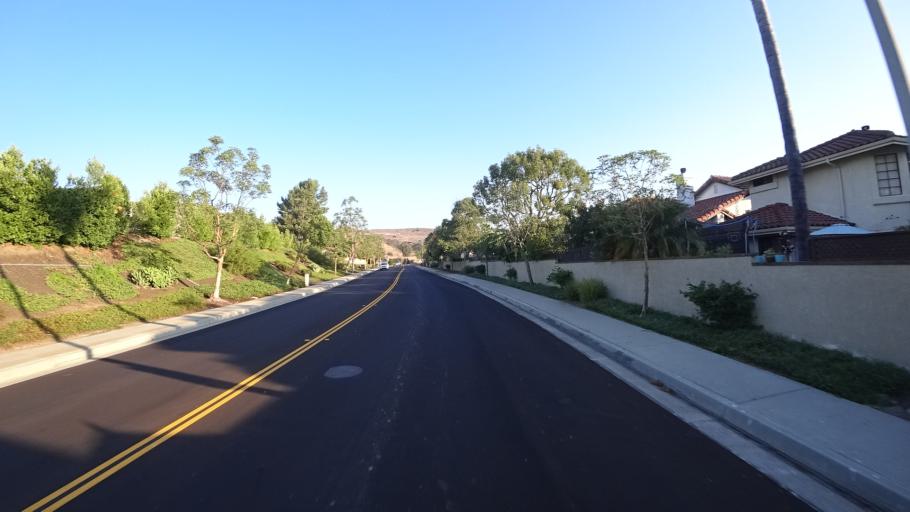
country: US
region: California
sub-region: Orange County
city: San Juan Capistrano
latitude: 33.4728
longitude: -117.6359
